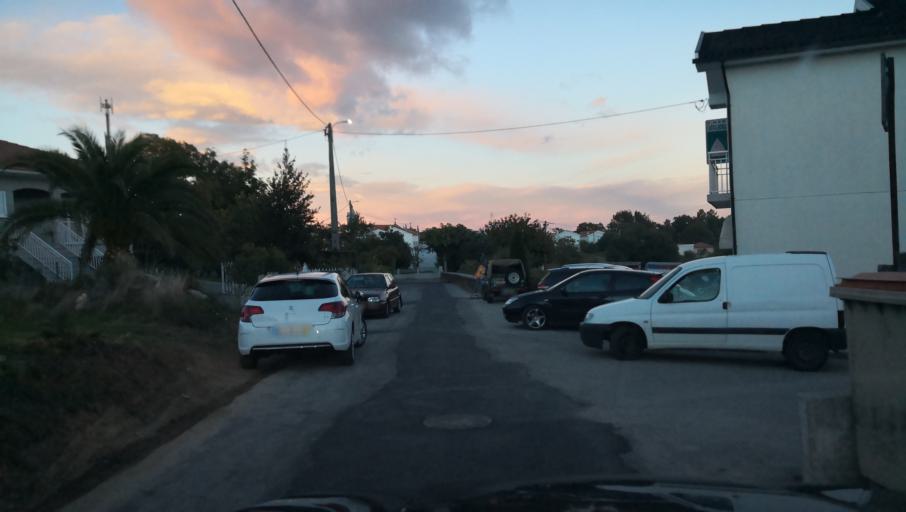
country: PT
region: Vila Real
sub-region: Santa Marta de Penaguiao
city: Santa Marta de Penaguiao
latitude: 41.2723
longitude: -7.8157
